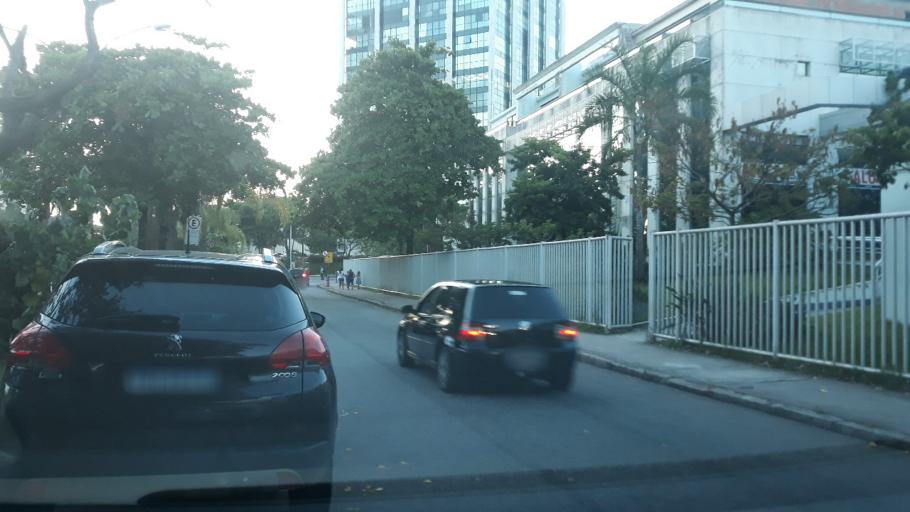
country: BR
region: Rio de Janeiro
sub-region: Rio De Janeiro
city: Rio de Janeiro
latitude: -23.0012
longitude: -43.3465
